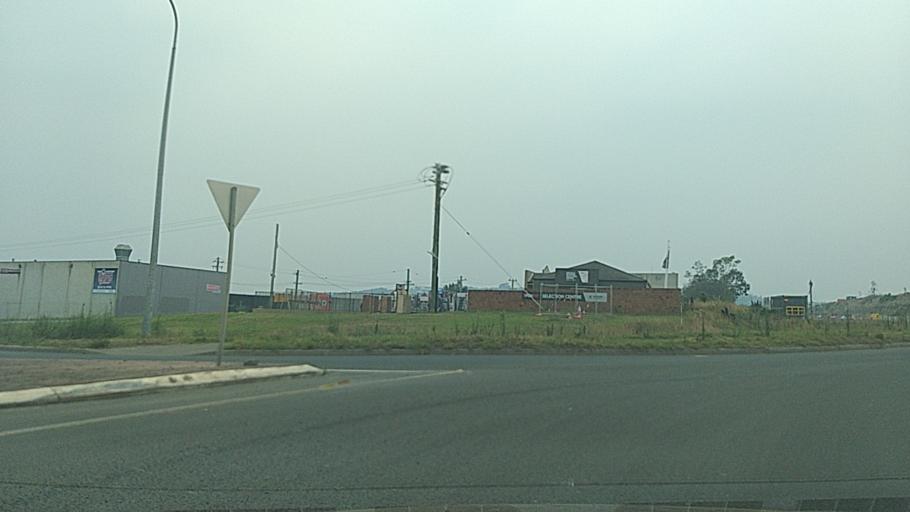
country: AU
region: New South Wales
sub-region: Shellharbour
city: Albion Park Rail
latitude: -34.5756
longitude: 150.8133
